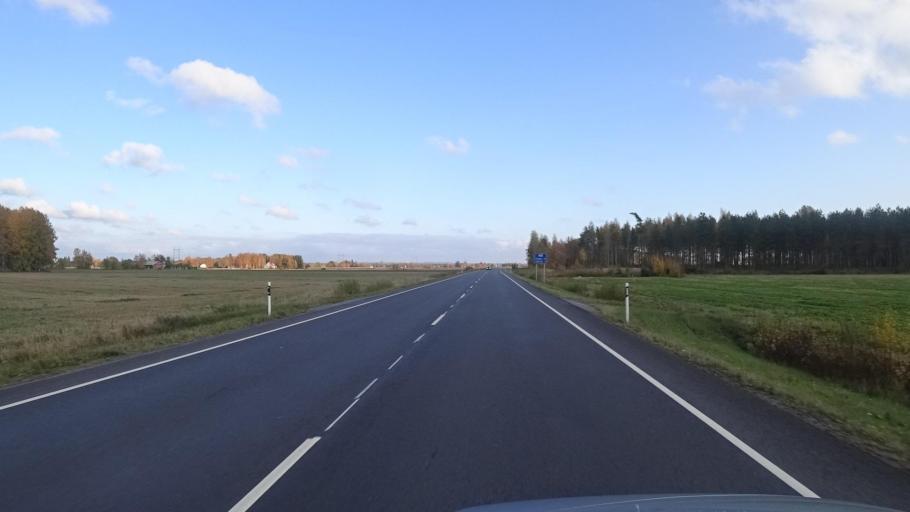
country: FI
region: Satakunta
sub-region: Rauma
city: Saekylae
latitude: 61.0719
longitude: 22.3074
